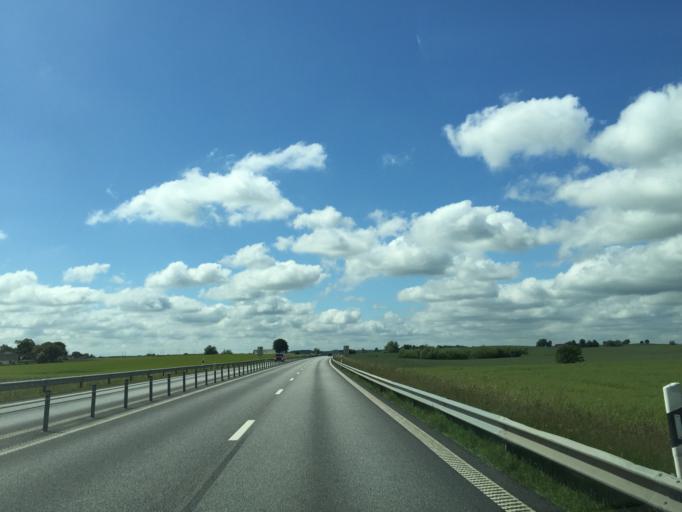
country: SE
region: Skane
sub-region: Skurups Kommun
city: Rydsgard
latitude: 55.4838
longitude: 13.5797
